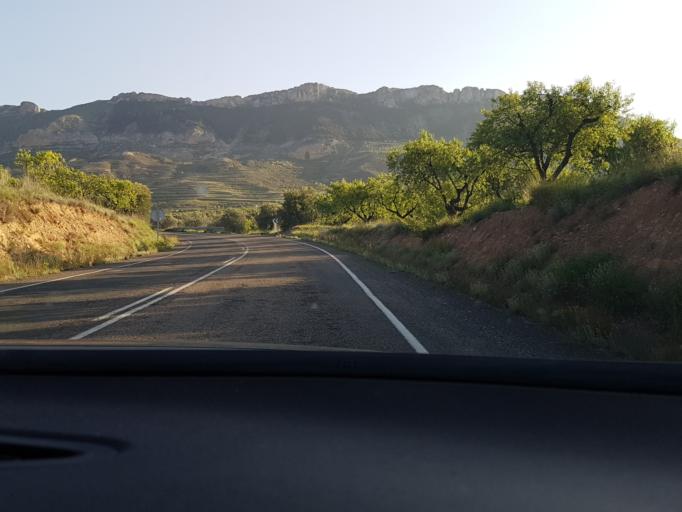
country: ES
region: La Rioja
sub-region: Provincia de La Rioja
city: Santa Eulalia Bajera
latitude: 42.2024
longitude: -2.1883
